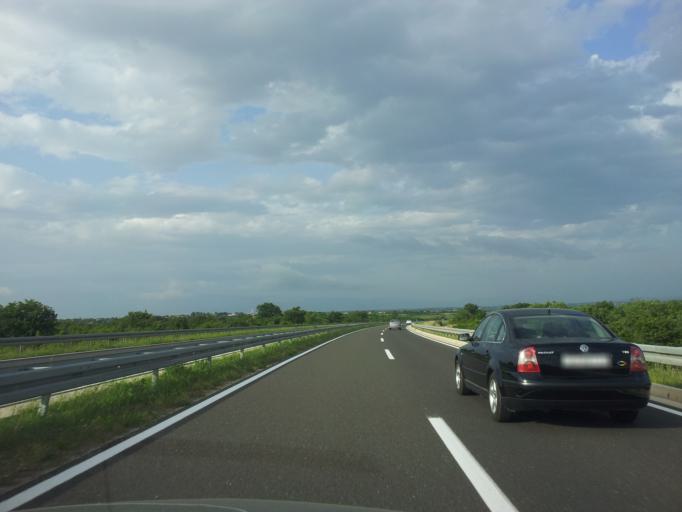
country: HR
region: Zadarska
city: Galovac
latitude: 44.0914
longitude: 15.3648
